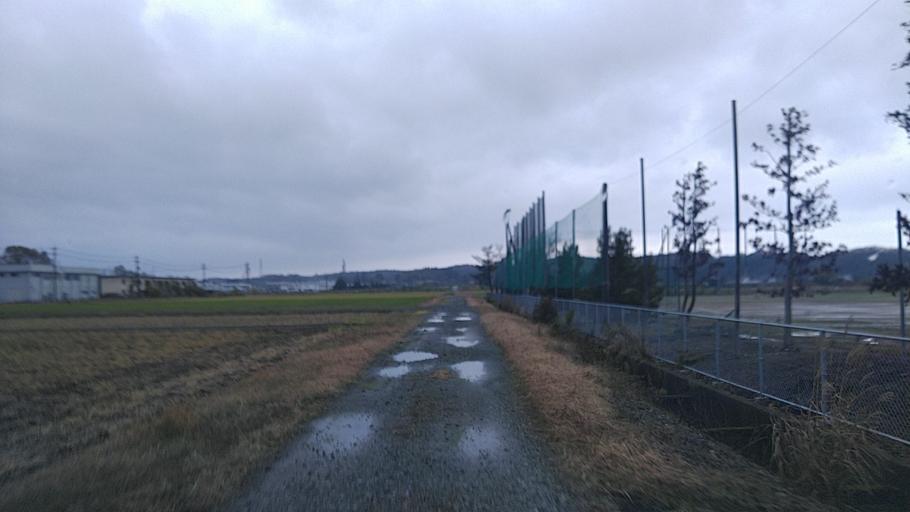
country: JP
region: Ishikawa
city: Komatsu
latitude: 36.3296
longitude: 136.3781
